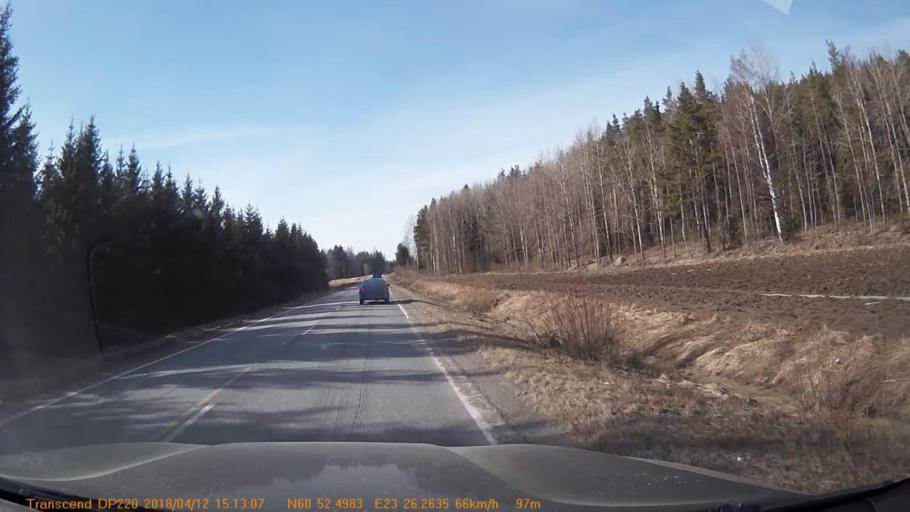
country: FI
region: Haeme
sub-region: Forssa
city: Jokioinen
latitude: 60.8751
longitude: 23.4376
